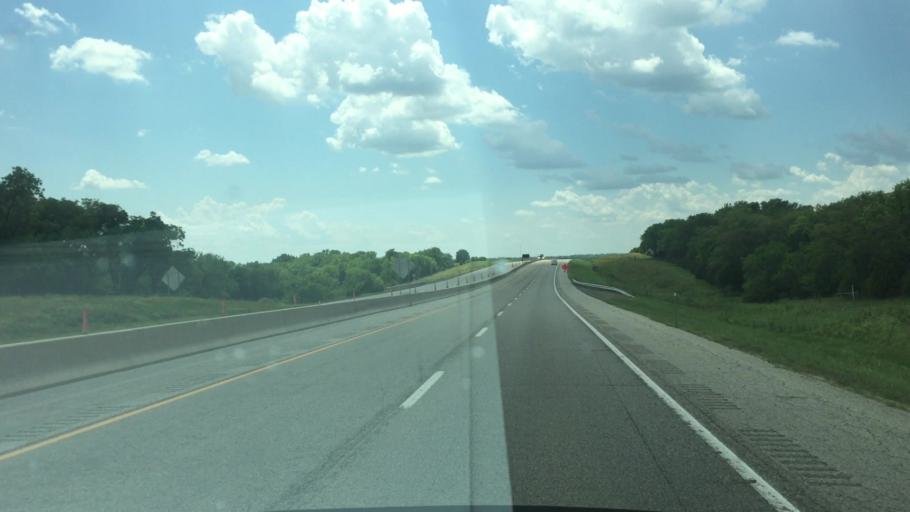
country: US
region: Kansas
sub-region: Shawnee County
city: Auburn
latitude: 38.9103
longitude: -95.7866
